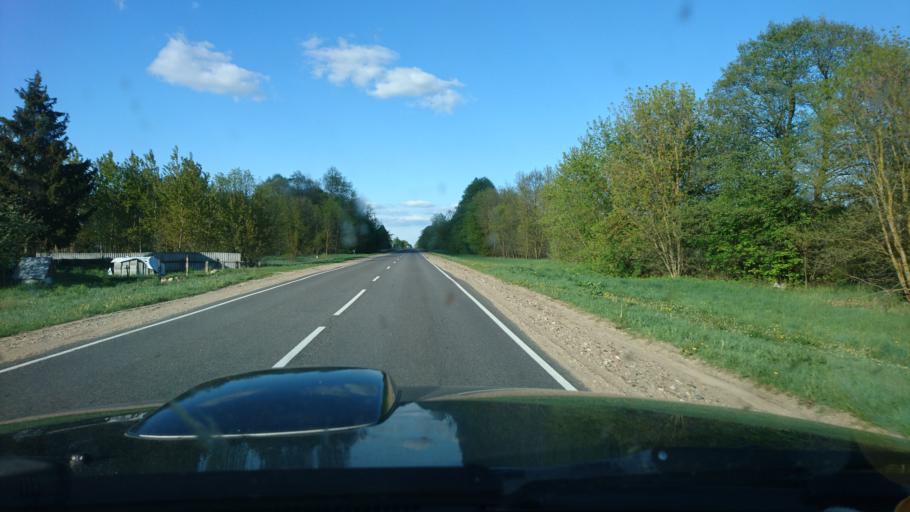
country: BY
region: Brest
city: Nyakhachava
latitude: 52.6414
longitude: 25.2003
